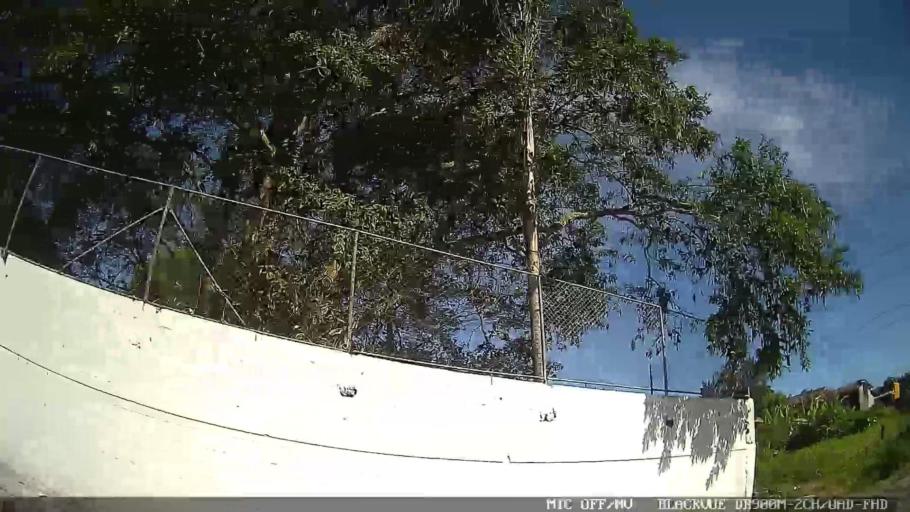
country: BR
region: Sao Paulo
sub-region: Santos
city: Santos
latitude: -23.9419
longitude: -46.2841
